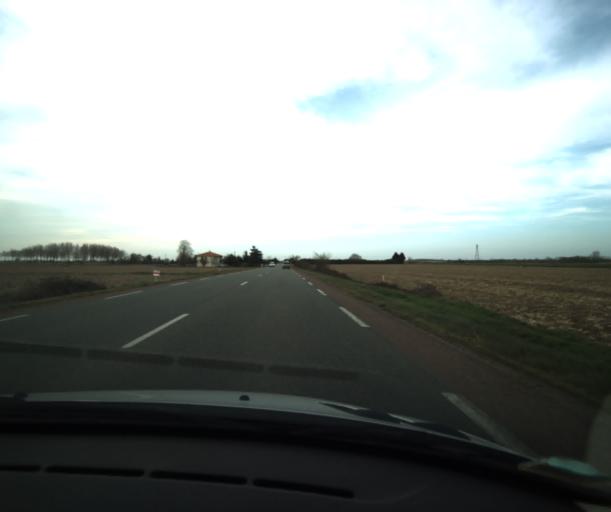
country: FR
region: Midi-Pyrenees
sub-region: Departement du Tarn-et-Garonne
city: Montech
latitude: 43.9705
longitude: 1.2051
